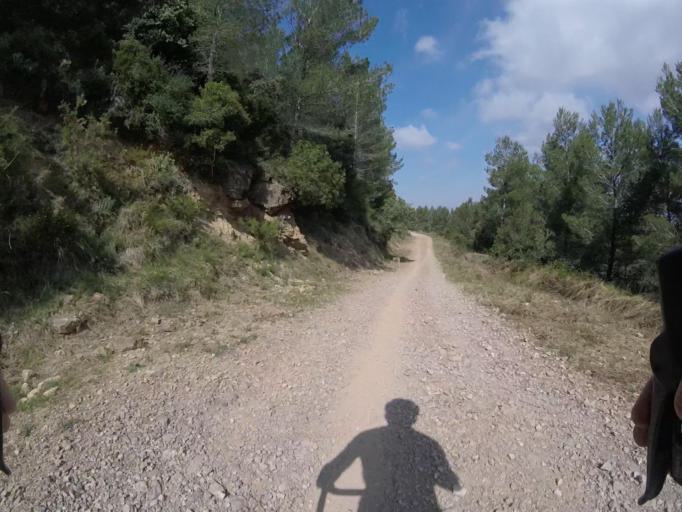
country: ES
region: Valencia
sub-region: Provincia de Castello
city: Benicassim
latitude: 40.0993
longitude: 0.0431
